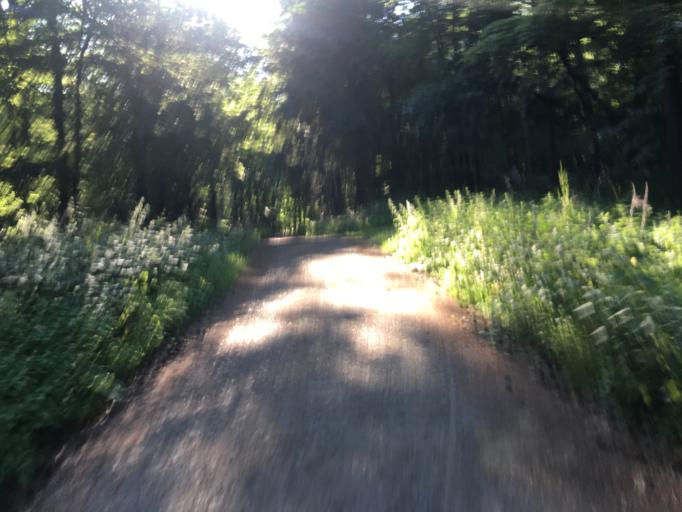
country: DE
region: Hesse
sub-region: Regierungsbezirk Darmstadt
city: Gelnhausen
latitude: 50.1685
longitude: 9.1557
